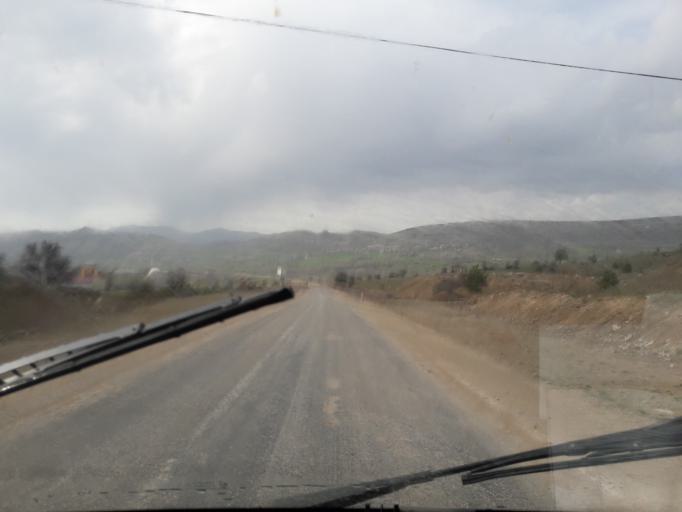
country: TR
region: Giresun
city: Alucra
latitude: 40.3206
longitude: 38.7737
